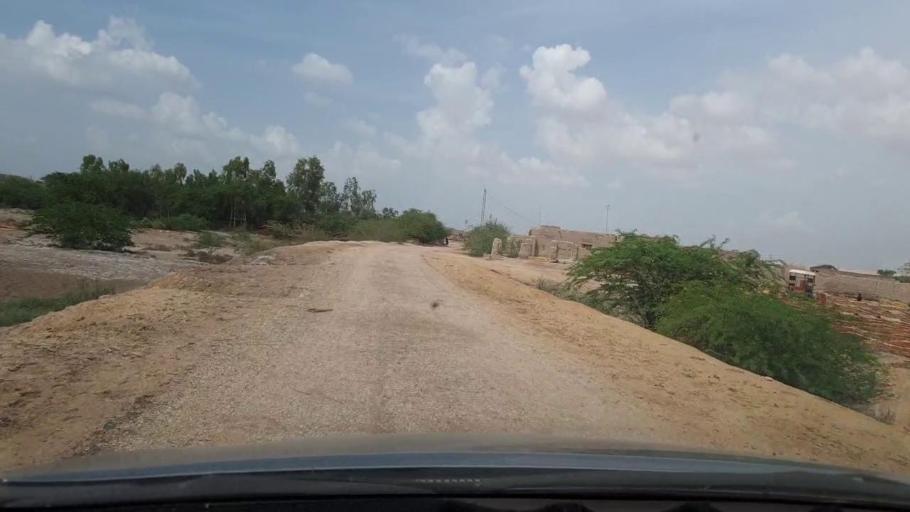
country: PK
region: Sindh
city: Khairpur
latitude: 27.4727
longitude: 68.8542
